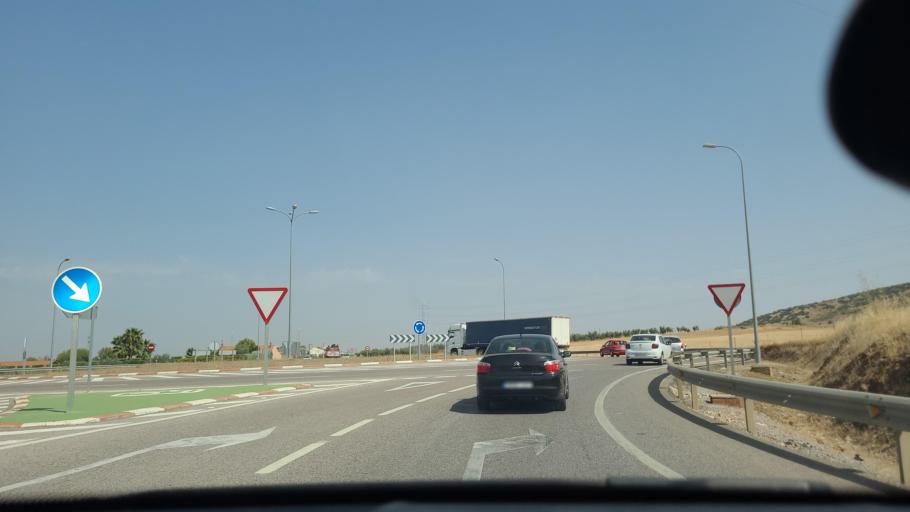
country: ES
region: Extremadura
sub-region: Provincia de Badajoz
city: Zafra
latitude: 38.4390
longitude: -6.4240
